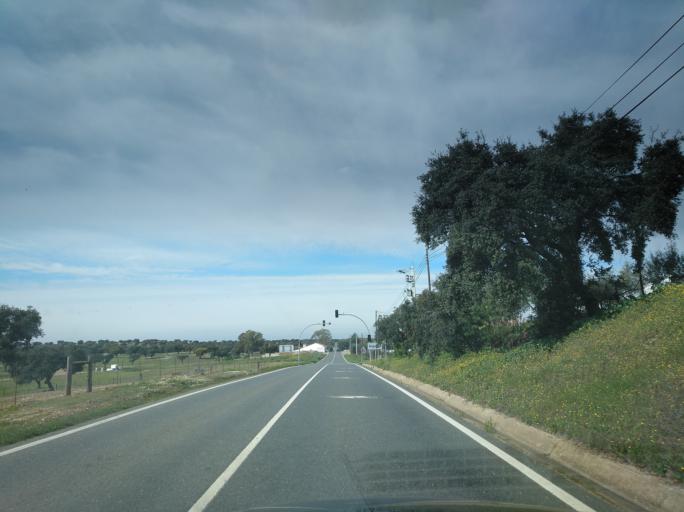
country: PT
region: Beja
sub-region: Mertola
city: Mertola
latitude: 37.7424
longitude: -7.7915
